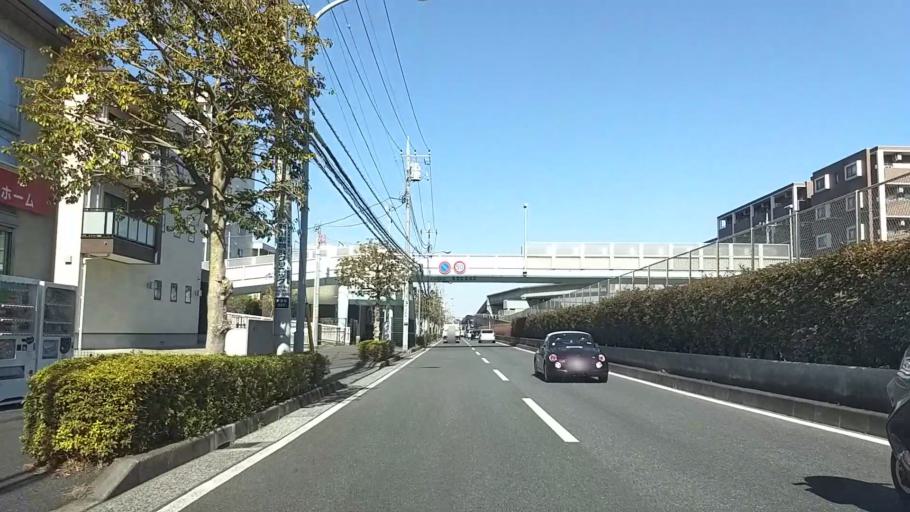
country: JP
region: Kanagawa
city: Yokohama
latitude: 35.5207
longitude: 139.6125
